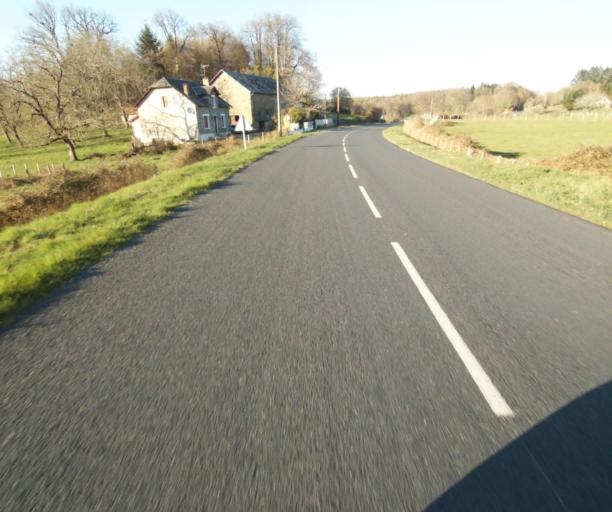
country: FR
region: Limousin
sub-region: Departement de la Correze
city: Saint-Clement
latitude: 45.3507
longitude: 1.7017
